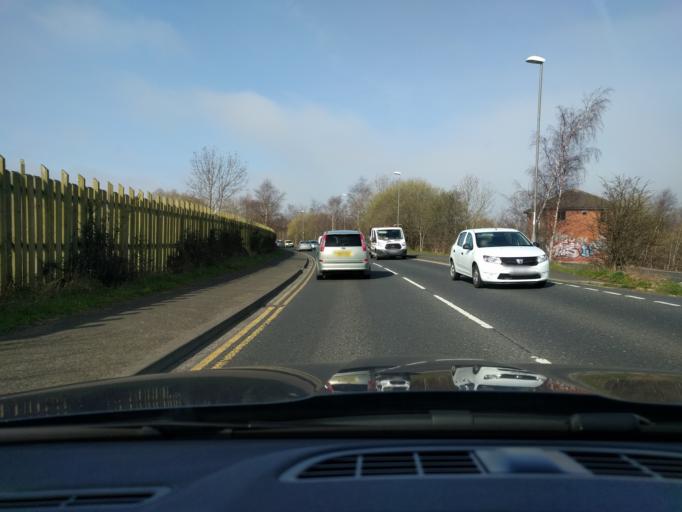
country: GB
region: England
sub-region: Newcastle upon Tyne
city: Benwell
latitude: 54.9590
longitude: -1.6505
